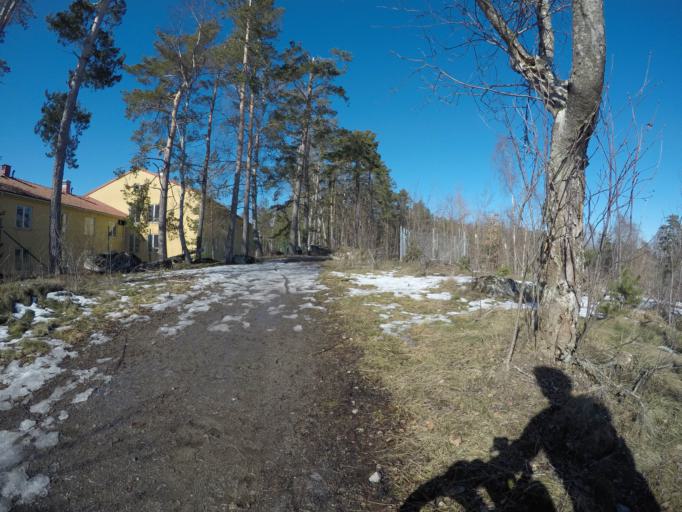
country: SE
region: Vaestmanland
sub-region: Vasteras
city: Vasteras
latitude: 59.5907
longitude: 16.6238
